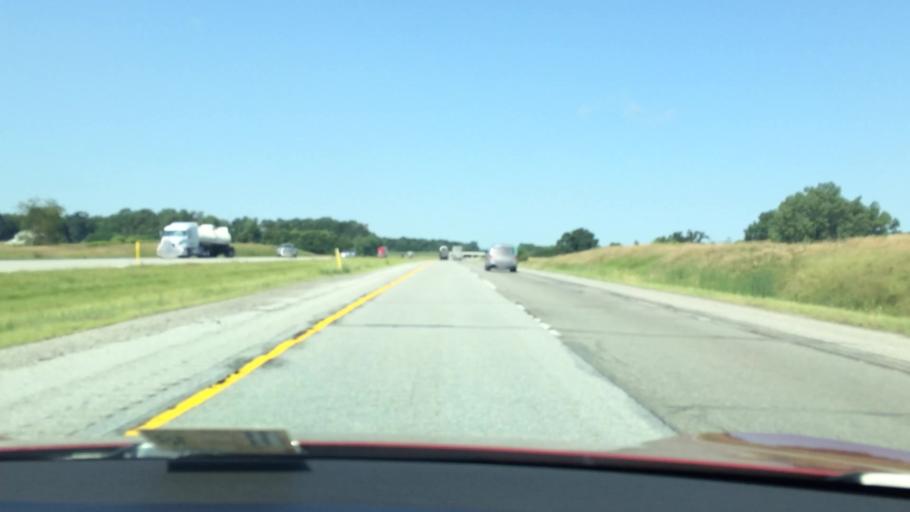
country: US
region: Michigan
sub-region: Saint Joseph County
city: White Pigeon
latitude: 41.7519
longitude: -85.6090
